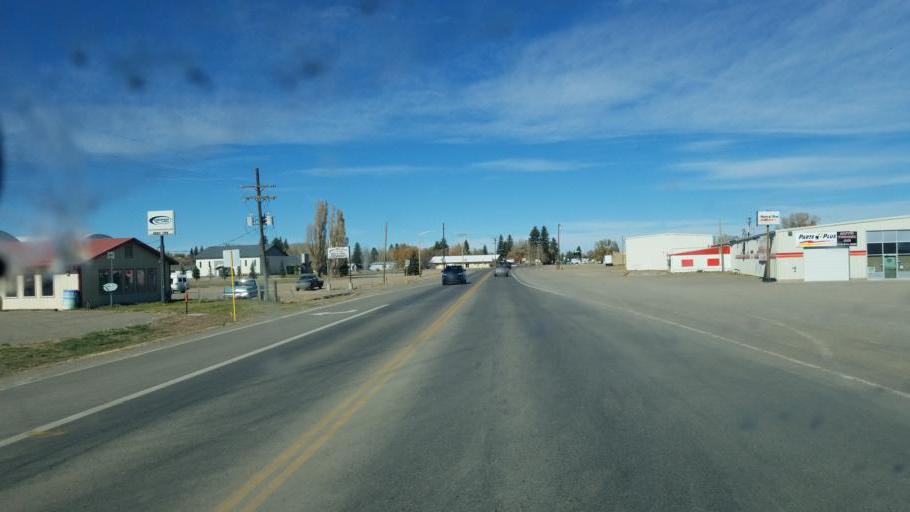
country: US
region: Colorado
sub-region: Conejos County
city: Conejos
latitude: 37.2695
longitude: -105.9628
